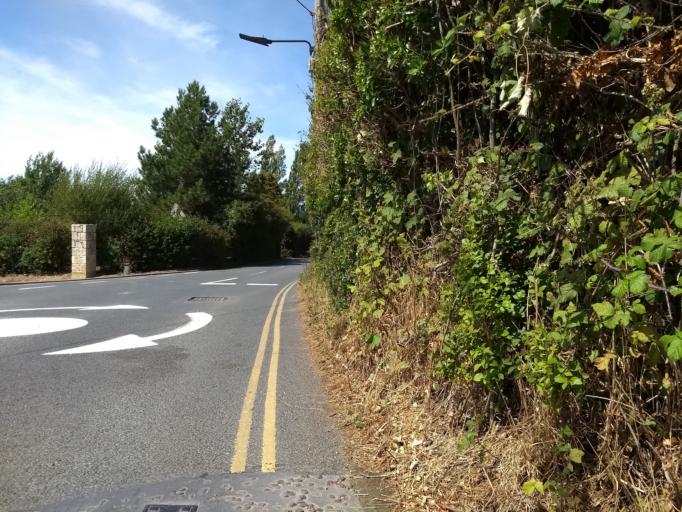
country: GB
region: England
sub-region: Isle of Wight
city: Gurnard
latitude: 50.7521
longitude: -1.3225
